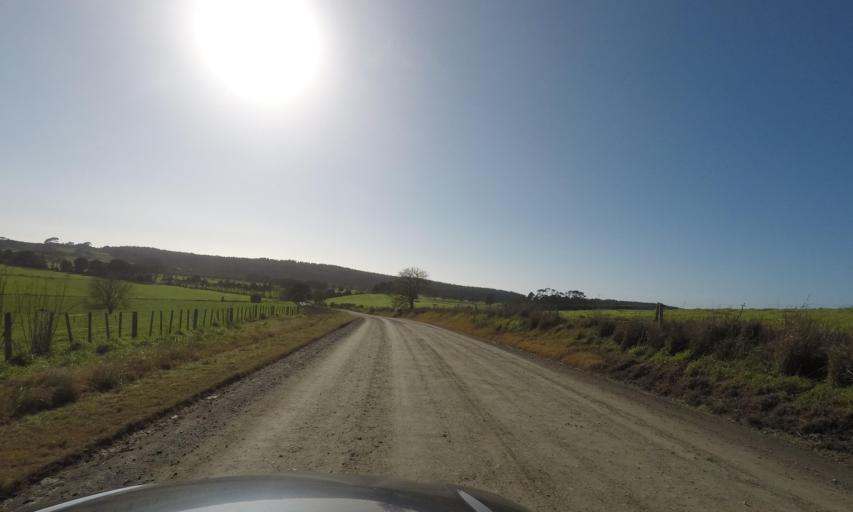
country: NZ
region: Auckland
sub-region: Auckland
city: Wellsford
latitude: -36.1599
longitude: 174.6109
